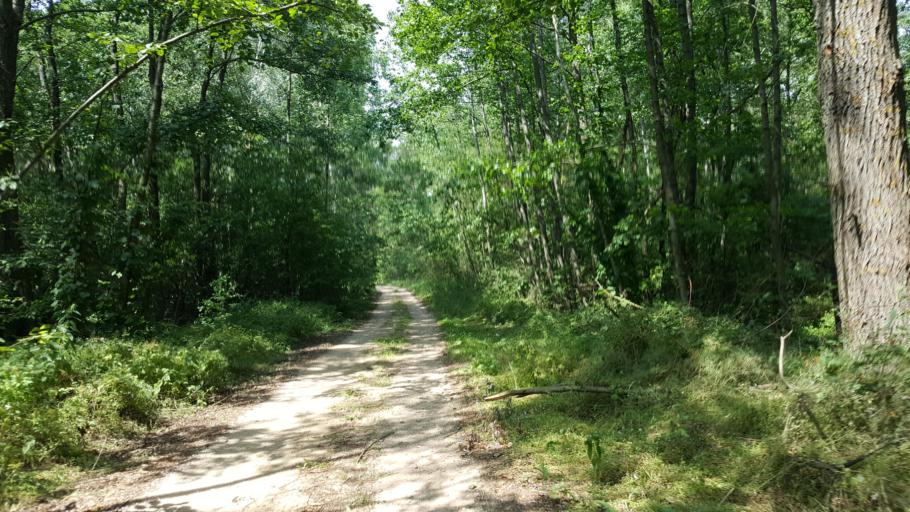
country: BY
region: Brest
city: Kamyanyets
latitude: 52.3672
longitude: 23.7515
